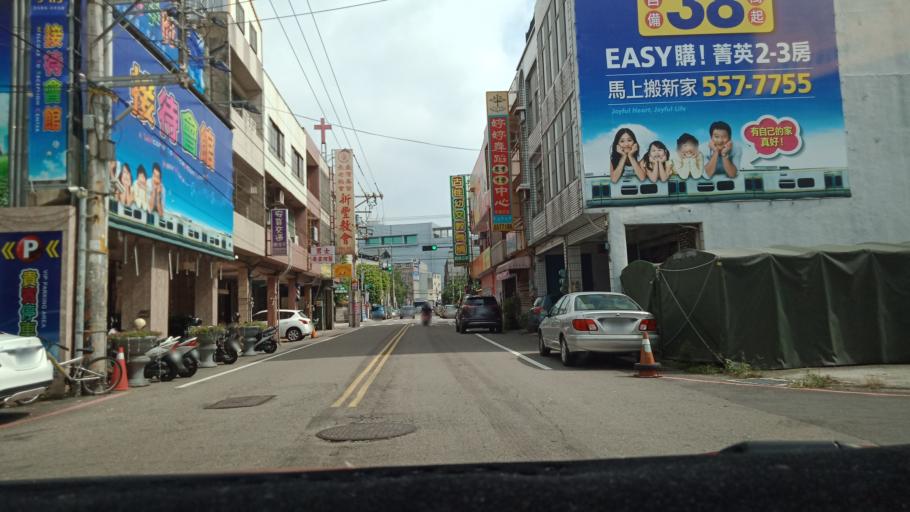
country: TW
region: Taiwan
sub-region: Hsinchu
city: Zhubei
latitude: 24.8725
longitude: 120.9965
